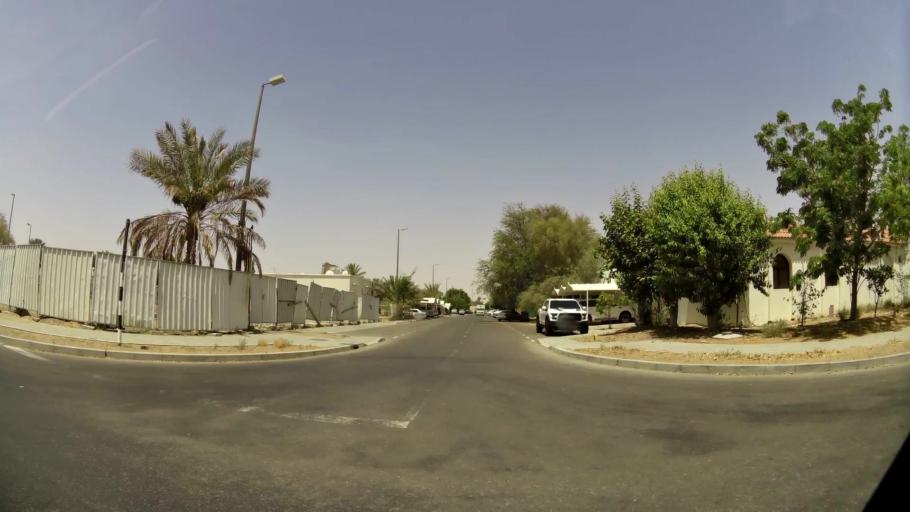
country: OM
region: Al Buraimi
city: Al Buraymi
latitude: 24.2715
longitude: 55.7434
